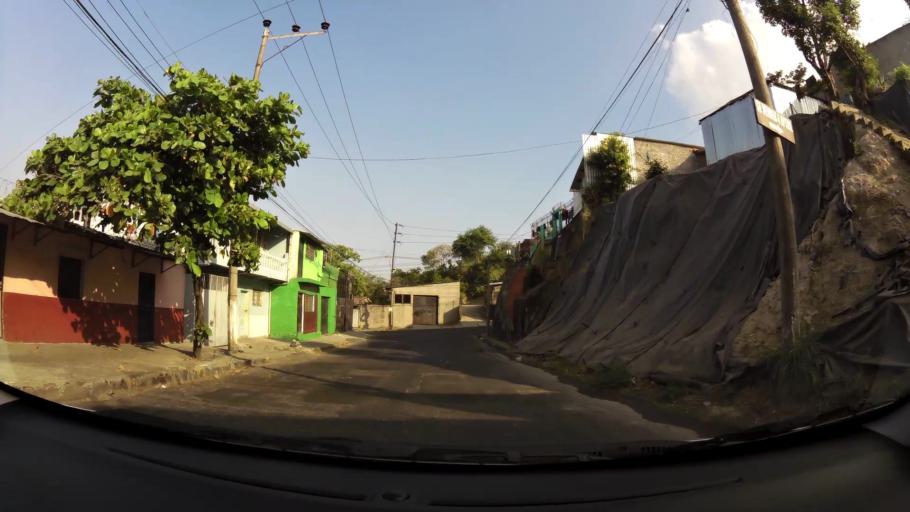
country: SV
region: San Salvador
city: San Salvador
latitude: 13.6970
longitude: -89.1775
